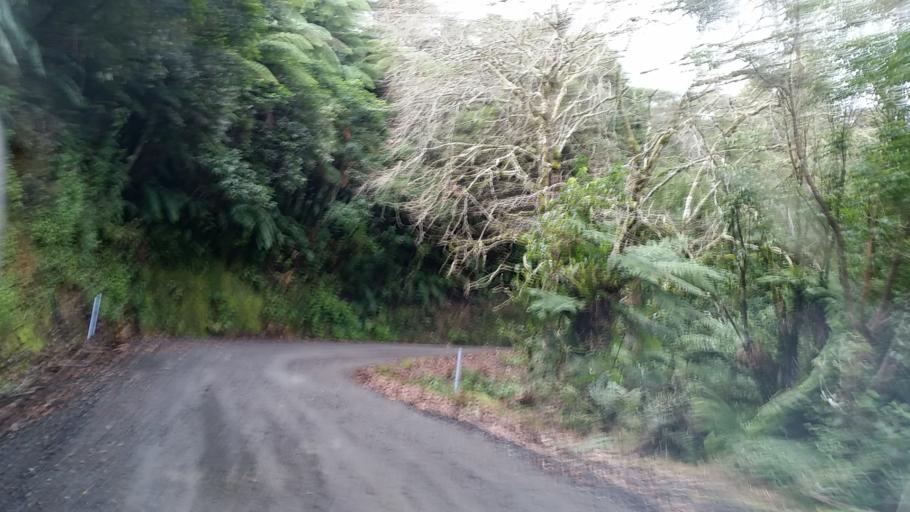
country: NZ
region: Taranaki
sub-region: New Plymouth District
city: Waitara
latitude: -39.1624
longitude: 174.5415
